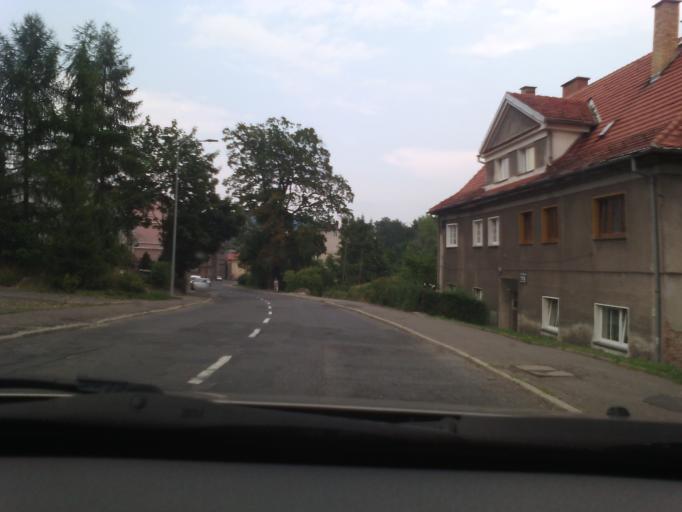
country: PL
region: Lower Silesian Voivodeship
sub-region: Powiat walbrzyski
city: Walbrzych
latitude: 50.7400
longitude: 16.2849
